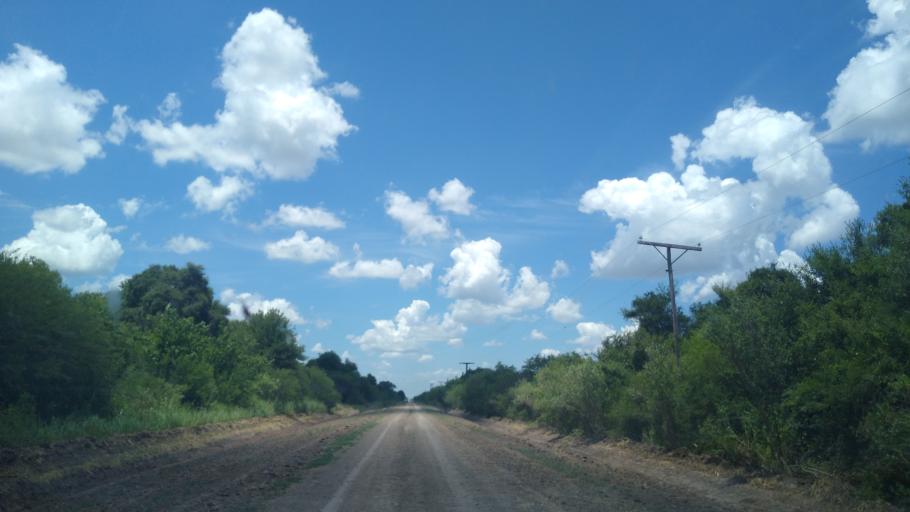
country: AR
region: Chaco
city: Presidencia Roque Saenz Pena
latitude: -26.7456
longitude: -60.3354
